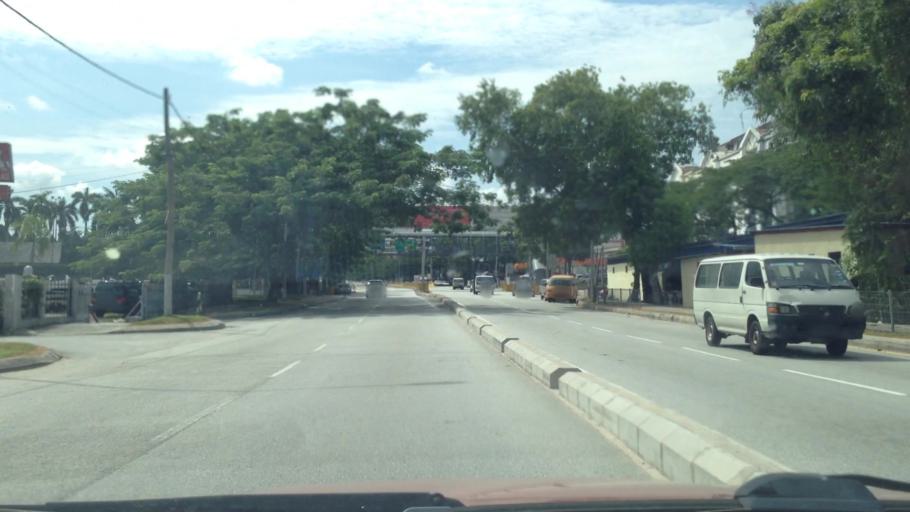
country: MY
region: Kuala Lumpur
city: Kuala Lumpur
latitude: 3.0920
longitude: 101.6853
